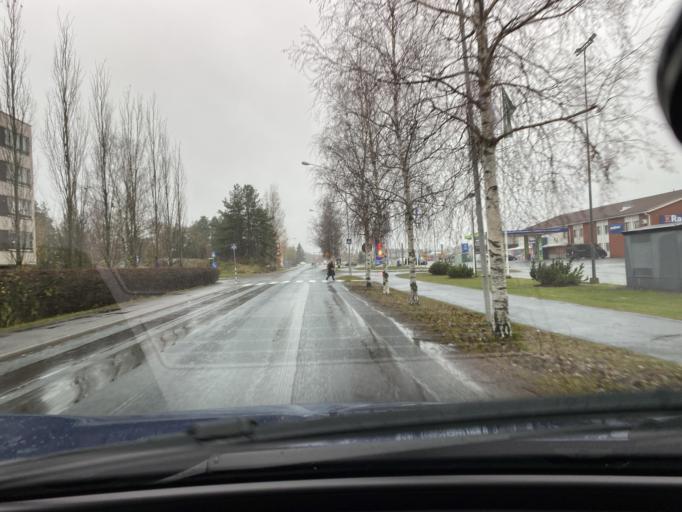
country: FI
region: Varsinais-Suomi
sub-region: Loimaa
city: Loimaa
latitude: 60.8558
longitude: 23.0465
